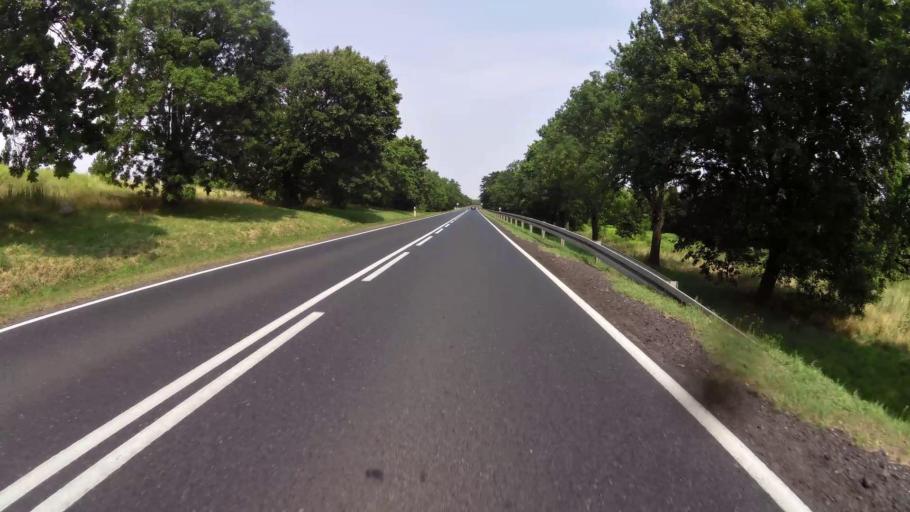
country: PL
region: West Pomeranian Voivodeship
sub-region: Powiat mysliborski
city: Mysliborz
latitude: 52.9308
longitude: 14.8895
